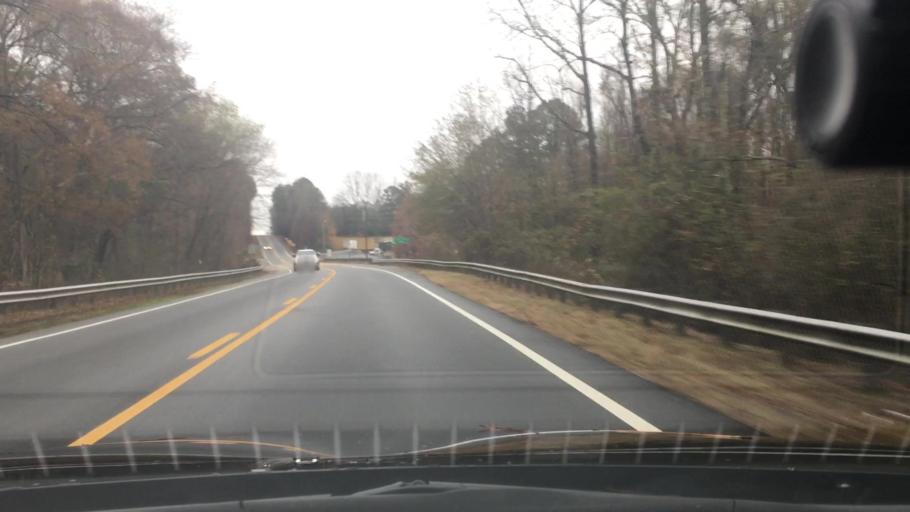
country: US
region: Georgia
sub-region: Coweta County
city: Senoia
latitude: 33.2570
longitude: -84.4988
